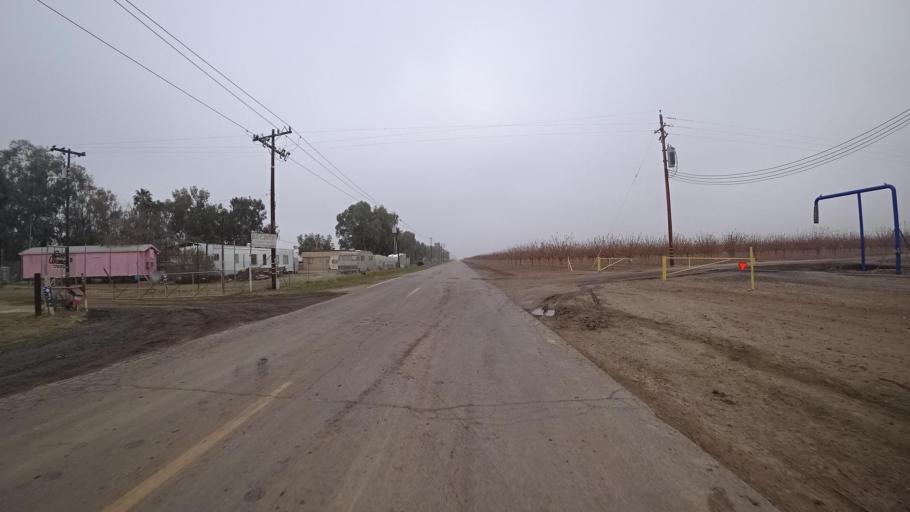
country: US
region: California
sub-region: Kern County
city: Wasco
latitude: 35.6880
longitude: -119.5087
